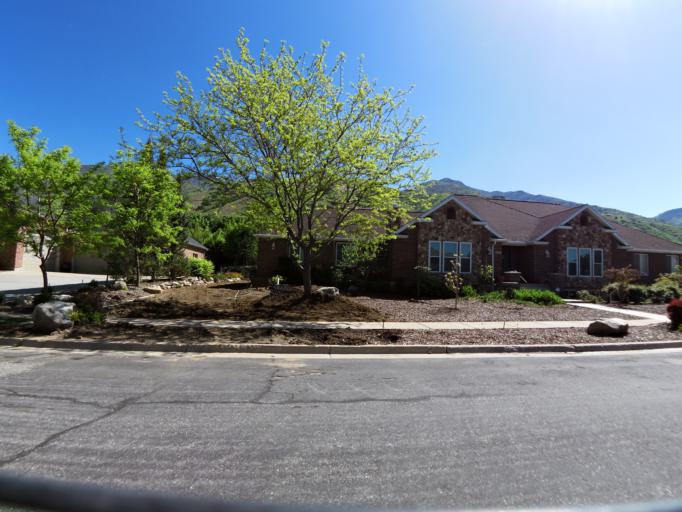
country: US
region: Utah
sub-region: Weber County
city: Uintah
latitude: 41.1660
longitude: -111.9275
